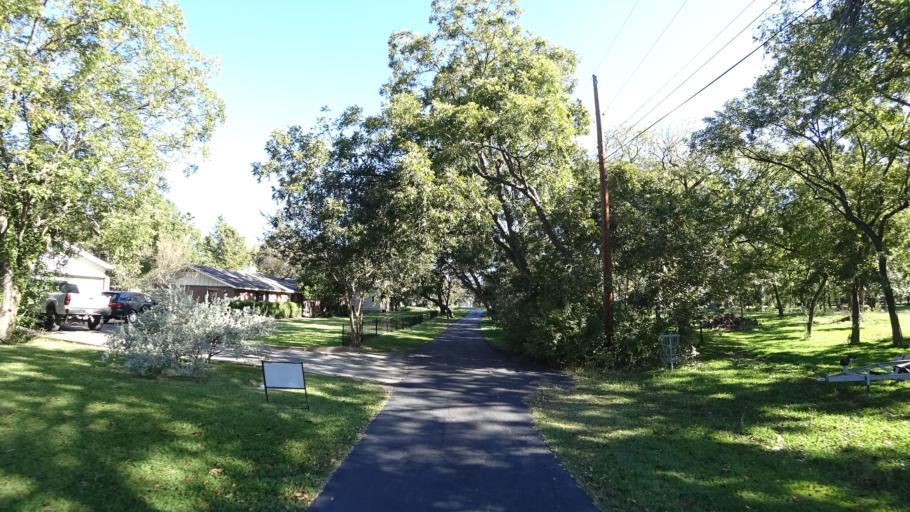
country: US
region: Texas
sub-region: Travis County
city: West Lake Hills
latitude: 30.3425
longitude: -97.7912
